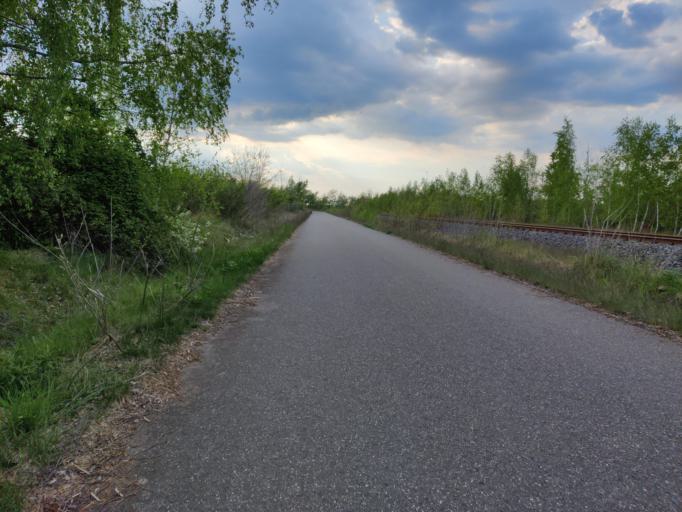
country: DE
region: Saxony
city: Rotha
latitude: 51.2126
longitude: 12.4364
